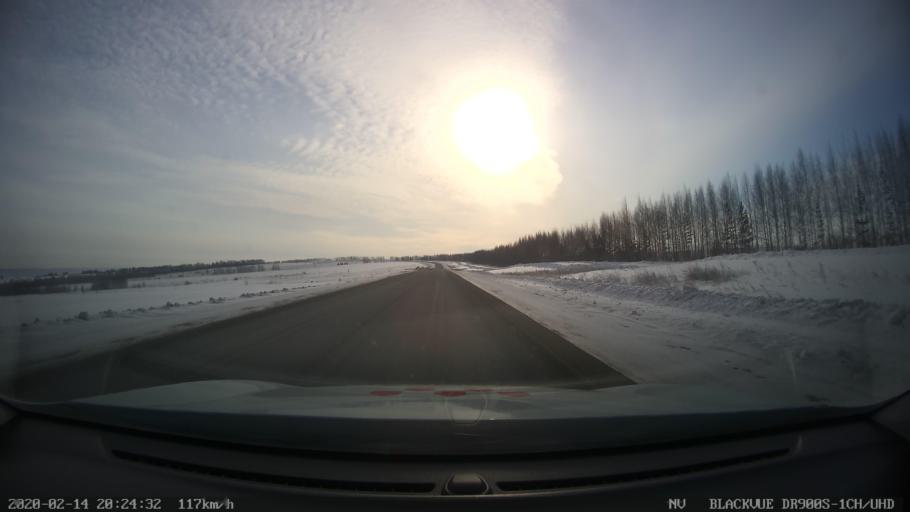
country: RU
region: Tatarstan
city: Verkhniy Uslon
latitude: 55.5116
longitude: 48.9711
